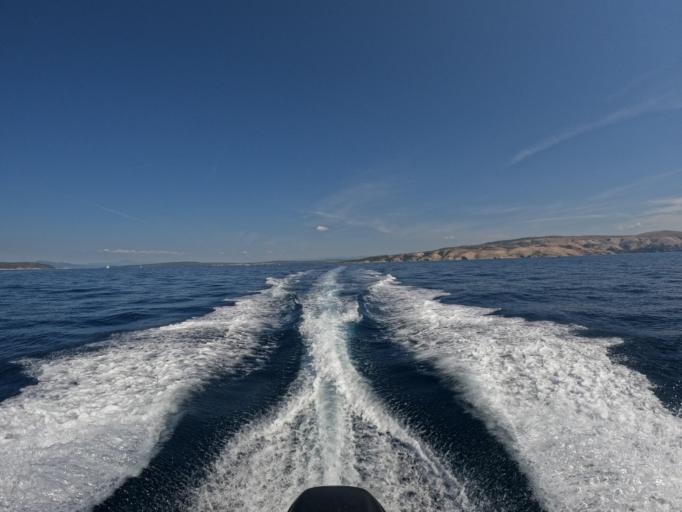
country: HR
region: Primorsko-Goranska
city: Punat
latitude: 44.9338
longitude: 14.6164
